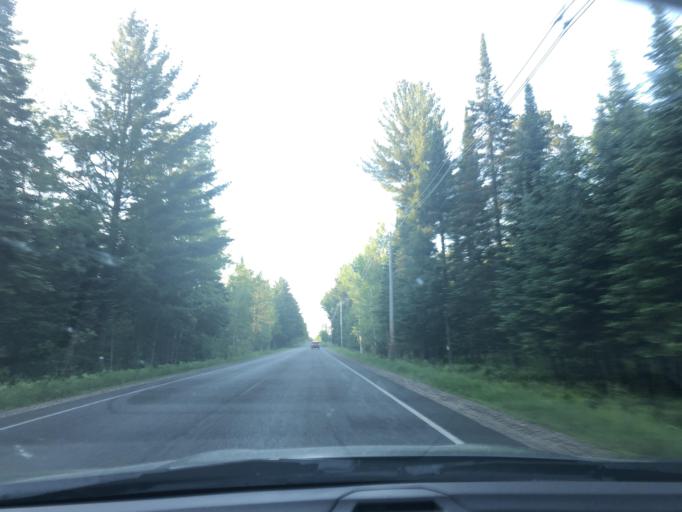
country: US
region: Michigan
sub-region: Missaukee County
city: Lake City
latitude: 44.3741
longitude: -85.0759
